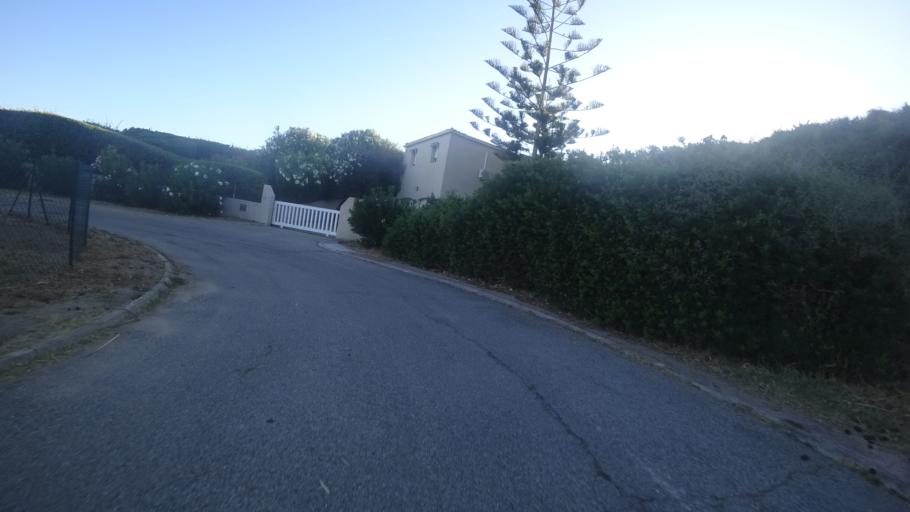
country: FR
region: Corsica
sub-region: Departement de la Corse-du-Sud
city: Alata
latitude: 41.9809
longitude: 8.6682
